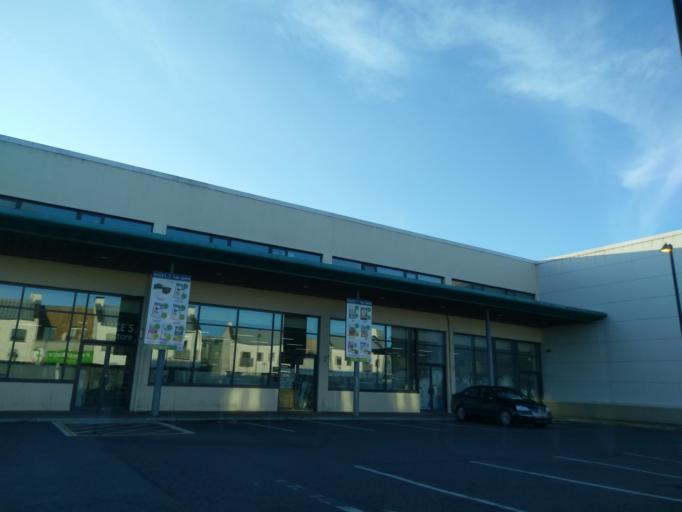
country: IE
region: Connaught
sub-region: County Galway
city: Athenry
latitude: 53.2931
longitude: -8.7506
